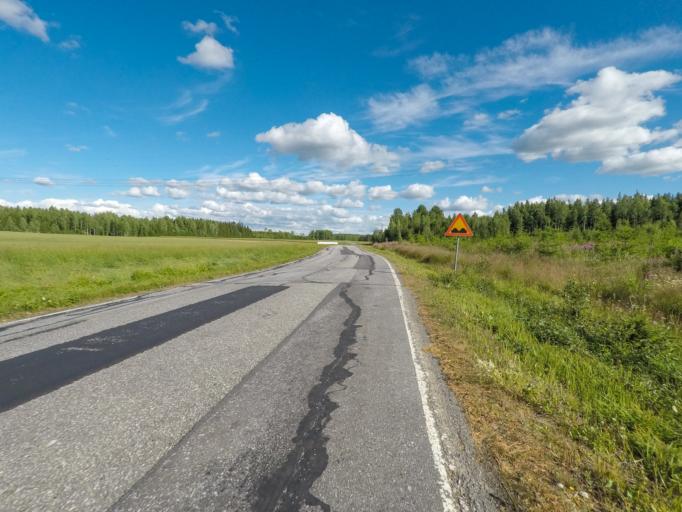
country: FI
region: South Karelia
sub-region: Imatra
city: Imatra
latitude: 61.1387
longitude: 28.6480
